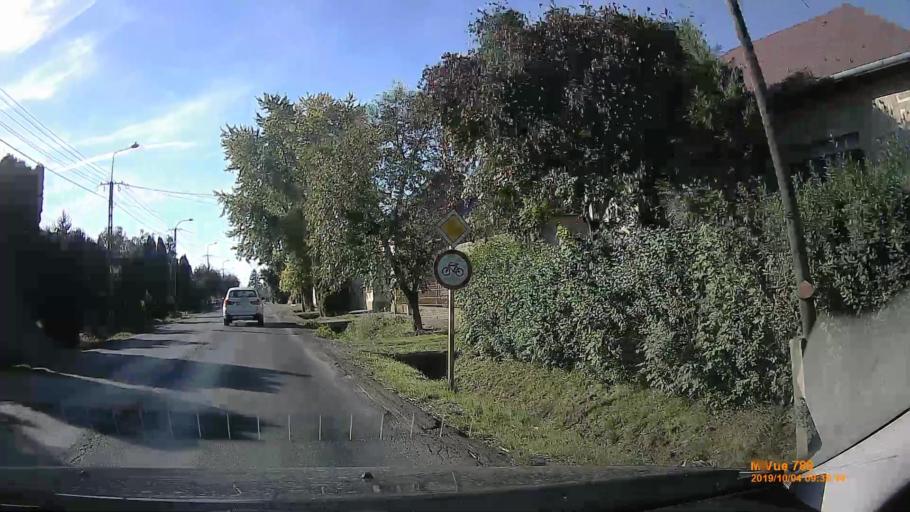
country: HU
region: Somogy
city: Kaposvar
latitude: 46.4607
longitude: 17.8051
